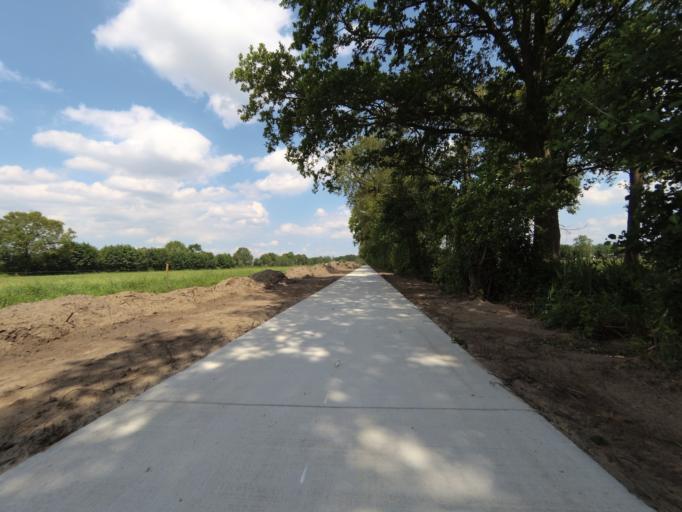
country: NL
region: Utrecht
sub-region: Gemeente Leusden
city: Leusden
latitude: 52.1090
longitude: 5.4188
